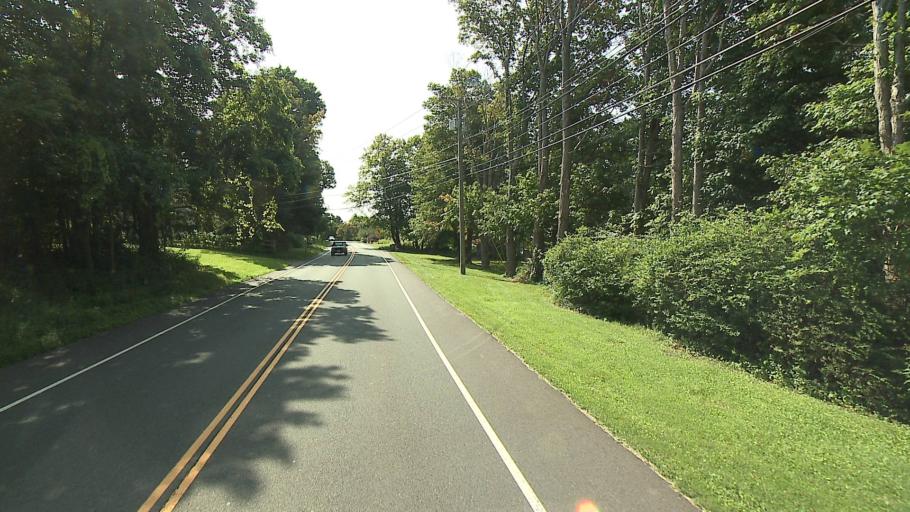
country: US
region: Connecticut
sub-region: Fairfield County
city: Newtown
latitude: 41.4449
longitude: -73.3749
